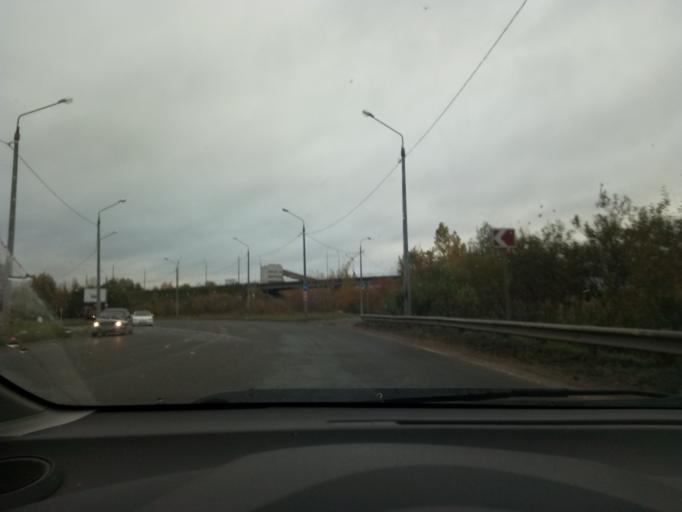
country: RU
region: Tatarstan
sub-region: Gorod Kazan'
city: Kazan
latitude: 55.8487
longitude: 49.1302
